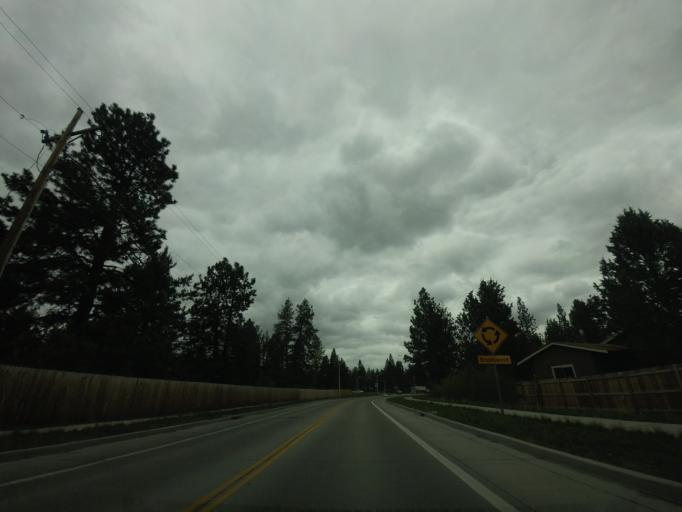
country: US
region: Oregon
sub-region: Deschutes County
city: Bend
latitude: 44.0202
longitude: -121.3280
